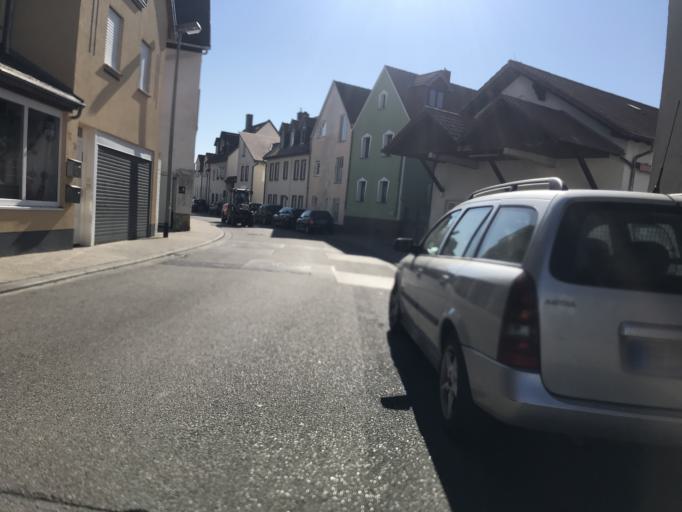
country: DE
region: Rheinland-Pfalz
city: Harxheim
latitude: 49.9130
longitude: 8.2458
